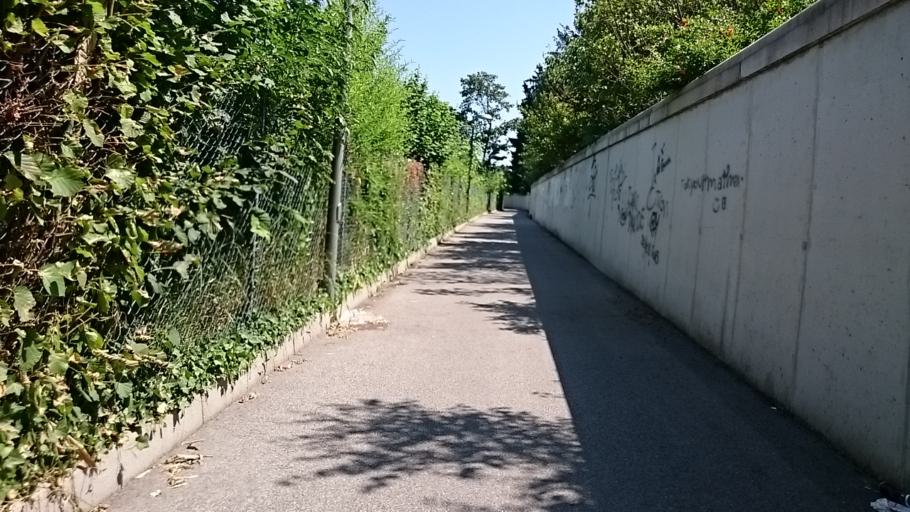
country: IT
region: Veneto
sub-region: Provincia di Padova
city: San Vito
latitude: 45.4142
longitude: 11.9596
